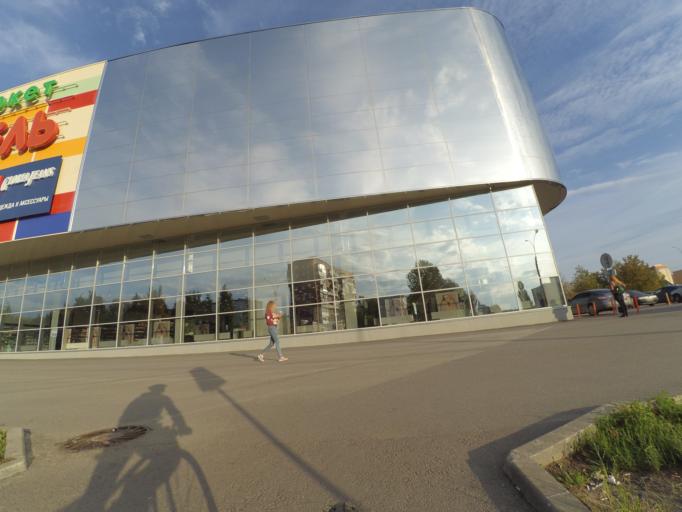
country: RU
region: Novgorod
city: Velikiy Novgorod
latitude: 58.5312
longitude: 31.2411
